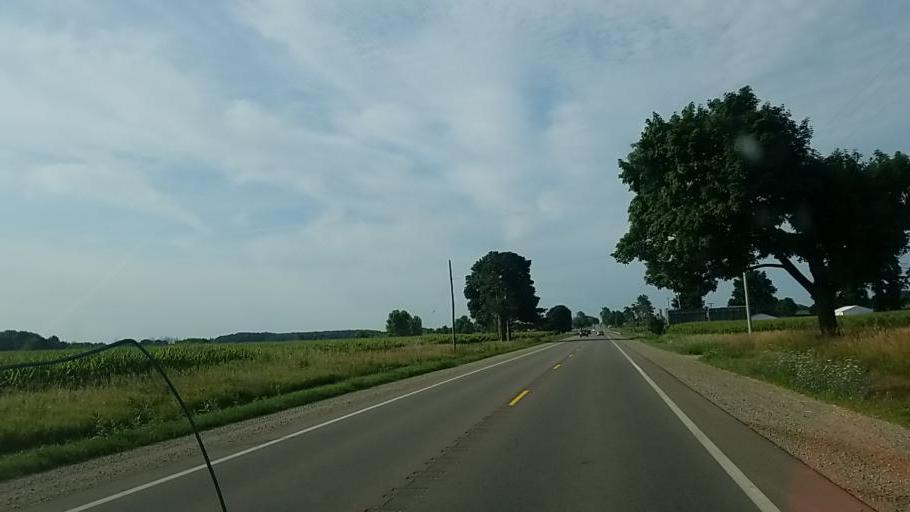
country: US
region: Michigan
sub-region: Ionia County
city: Ionia
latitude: 42.9214
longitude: -85.0748
